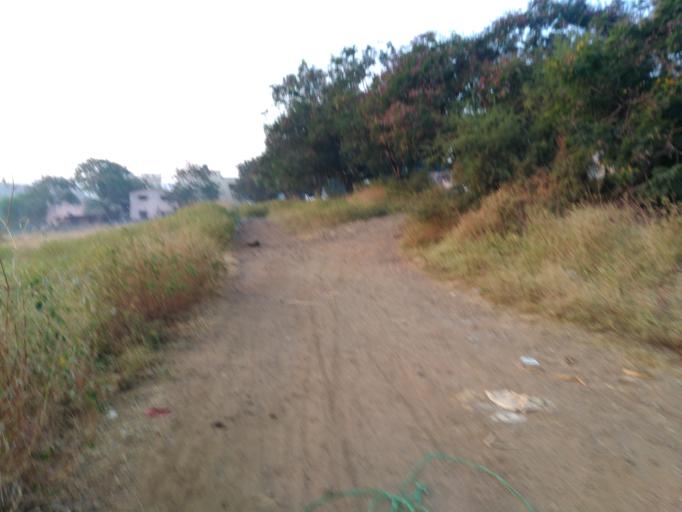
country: IN
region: Maharashtra
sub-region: Pune Division
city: Pune
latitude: 18.4541
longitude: 73.8946
